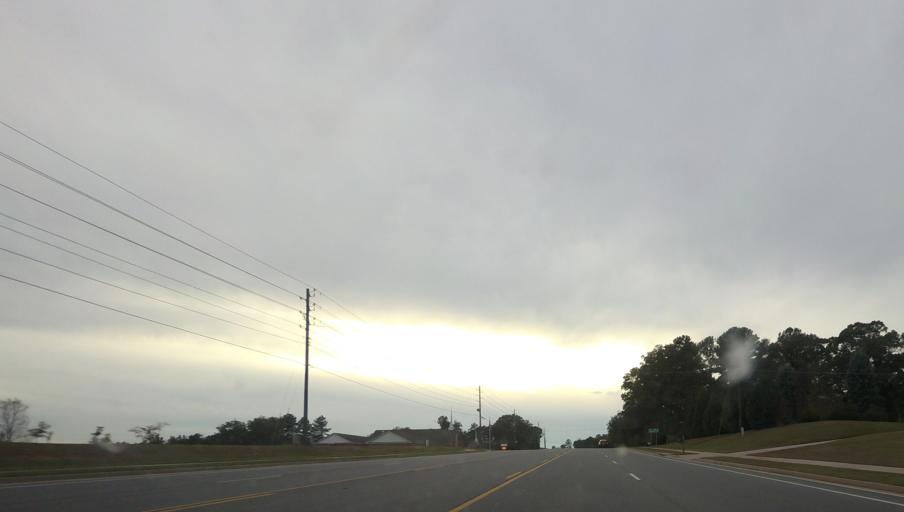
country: US
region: Georgia
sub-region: Houston County
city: Perry
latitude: 32.4979
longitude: -83.6698
